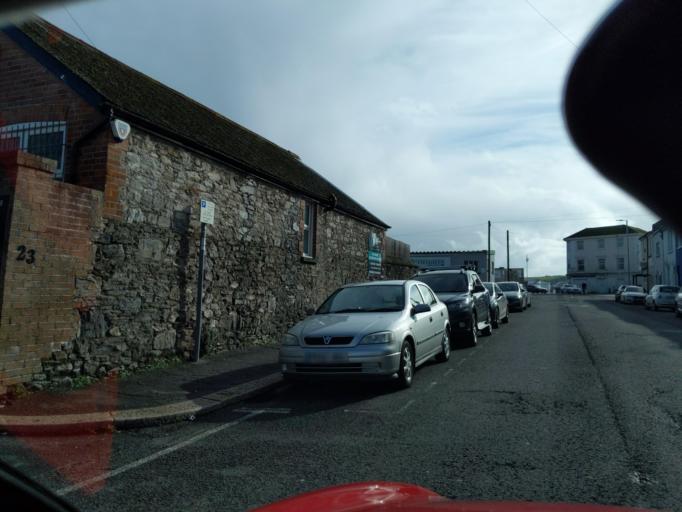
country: GB
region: England
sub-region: Plymouth
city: Plymouth
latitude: 50.3667
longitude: -4.1266
